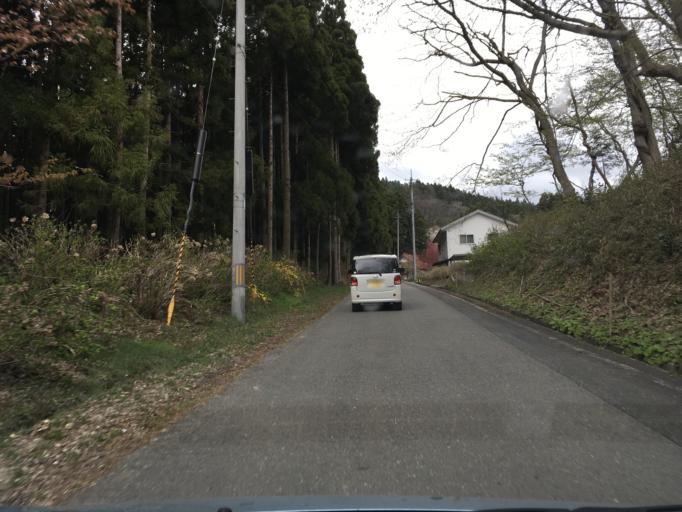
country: JP
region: Iwate
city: Ichinoseki
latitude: 38.9662
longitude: 141.1855
